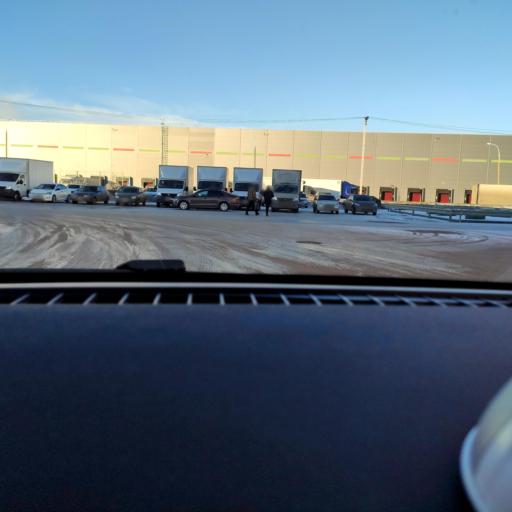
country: RU
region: Samara
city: Samara
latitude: 53.0921
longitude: 50.1287
